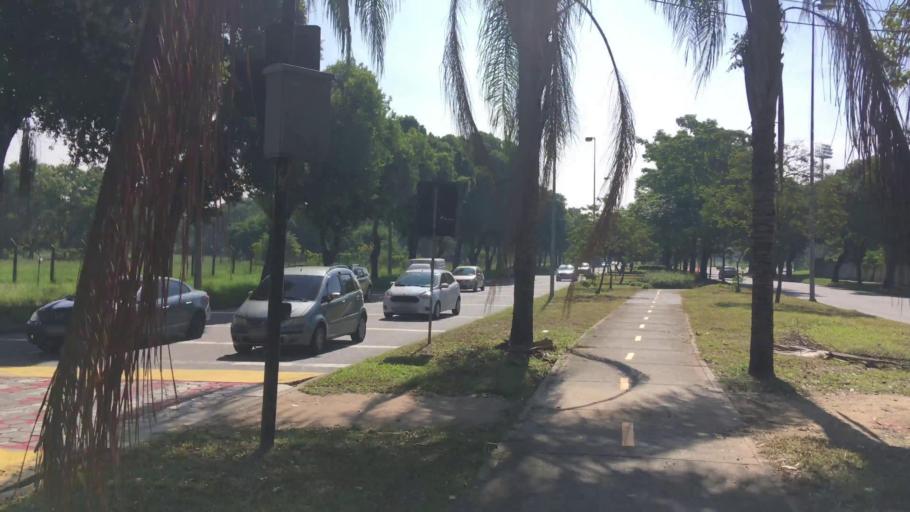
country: BR
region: Rio de Janeiro
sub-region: Rio De Janeiro
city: Rio de Janeiro
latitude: -22.8498
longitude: -43.2351
